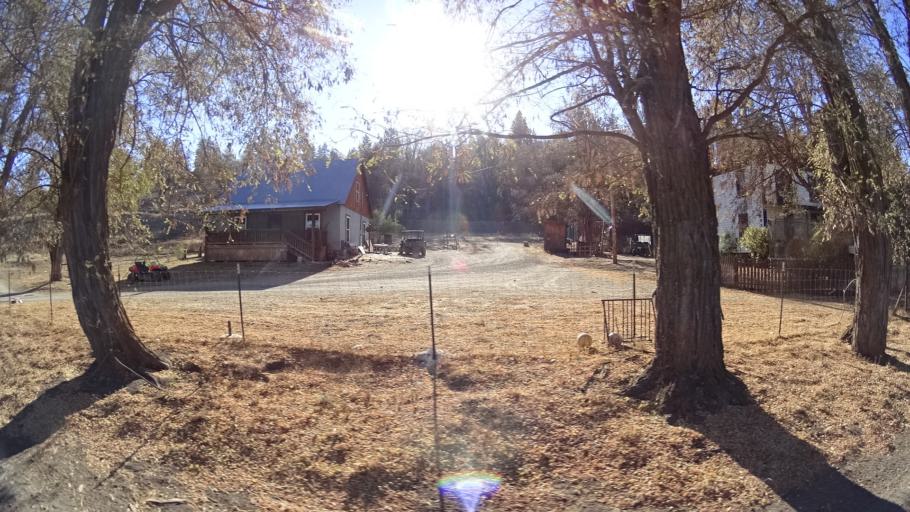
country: US
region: California
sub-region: Siskiyou County
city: Yreka
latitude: 41.5348
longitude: -122.8373
